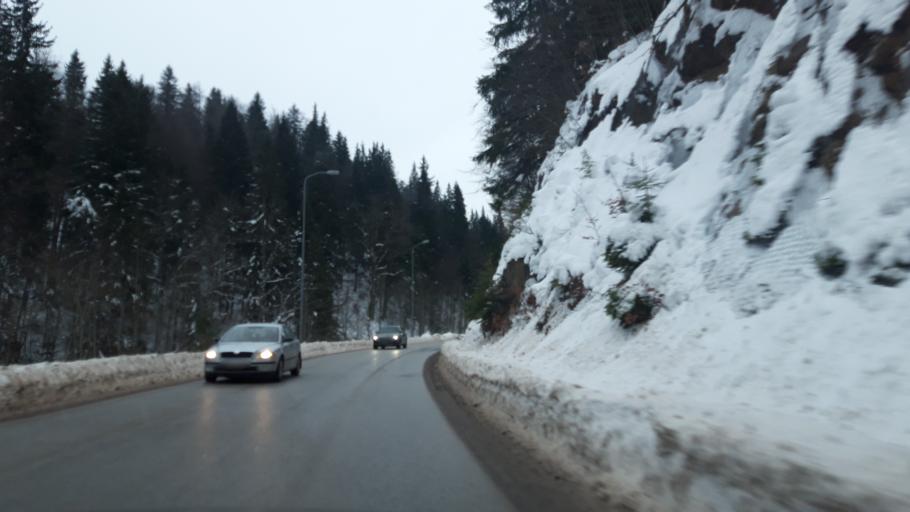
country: BA
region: Republika Srpska
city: Koran
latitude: 43.7412
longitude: 18.5688
